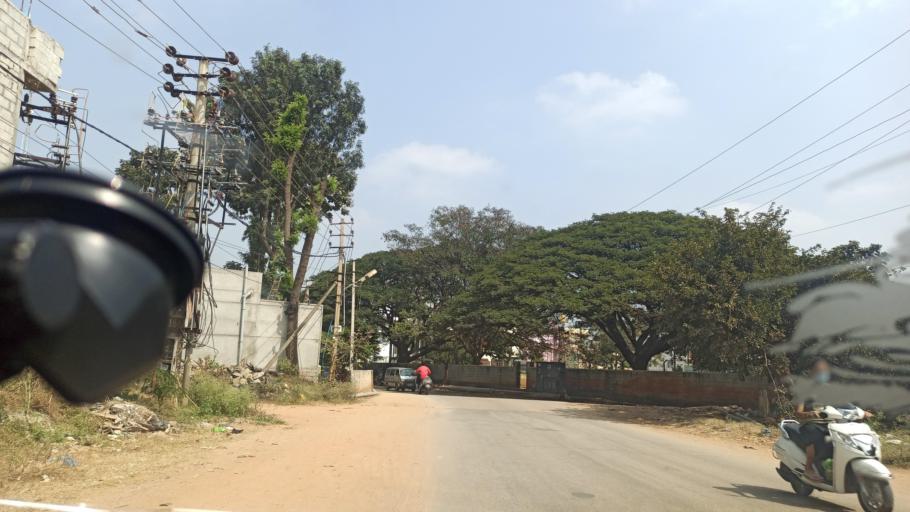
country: IN
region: Karnataka
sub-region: Bangalore Urban
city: Yelahanka
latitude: 13.0767
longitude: 77.6056
